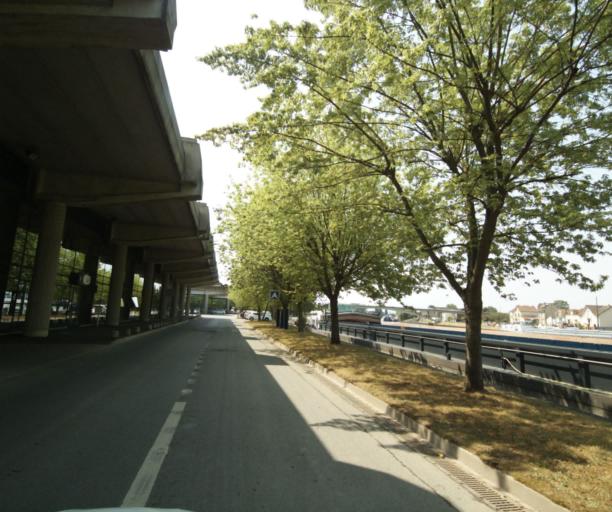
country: FR
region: Ile-de-France
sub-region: Departement des Yvelines
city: Maurecourt
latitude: 48.9915
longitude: 2.0730
